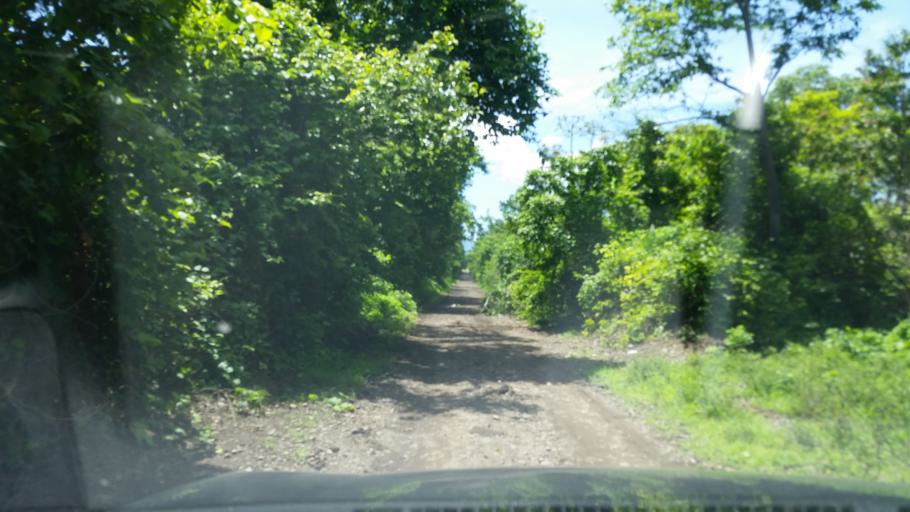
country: NI
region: Chinandega
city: Puerto Morazan
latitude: 12.7609
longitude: -87.1281
